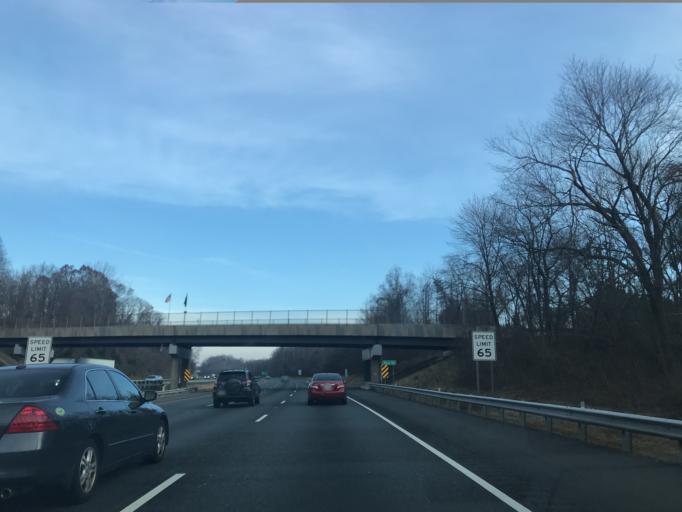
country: US
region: Maryland
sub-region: Harford County
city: Aberdeen
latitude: 39.5335
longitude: -76.1767
